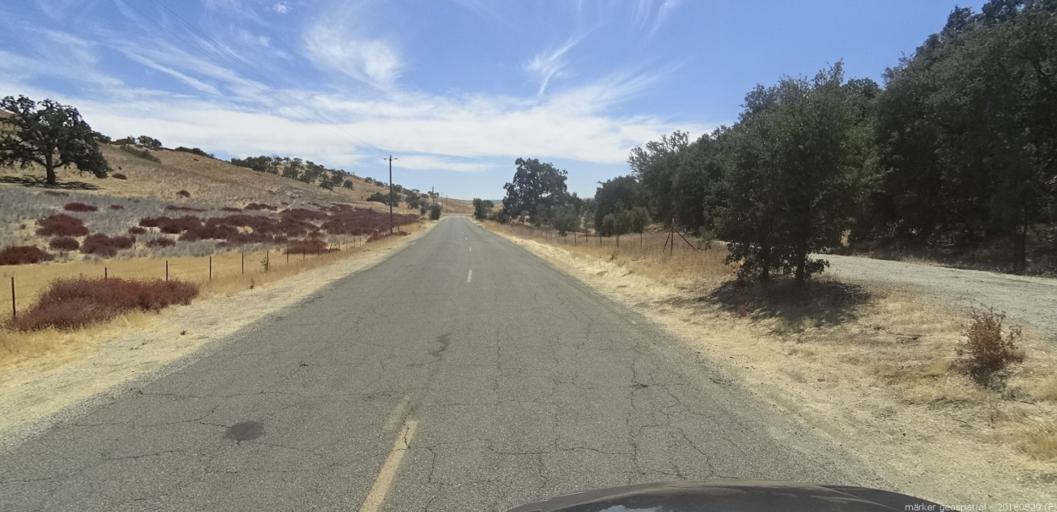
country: US
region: California
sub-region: San Luis Obispo County
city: Lake Nacimiento
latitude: 35.8828
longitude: -120.9926
